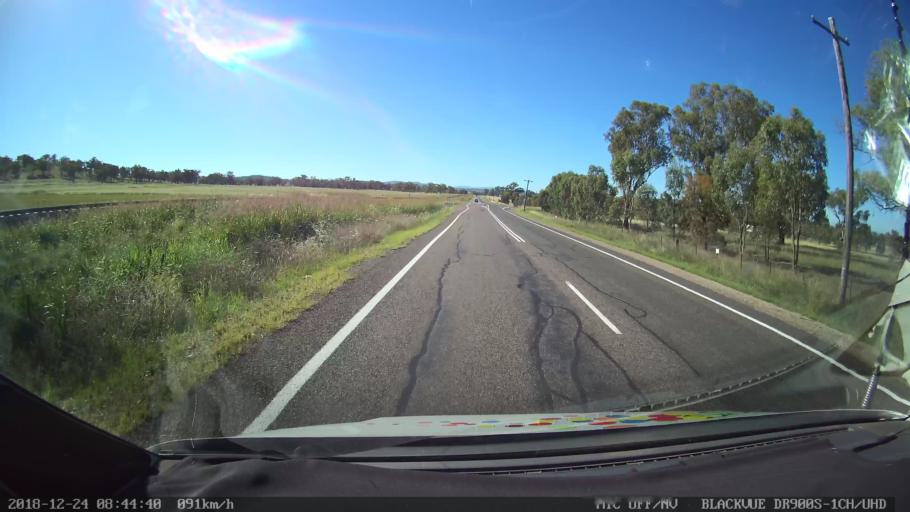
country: AU
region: New South Wales
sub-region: Liverpool Plains
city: Quirindi
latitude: -31.4050
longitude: 150.6487
